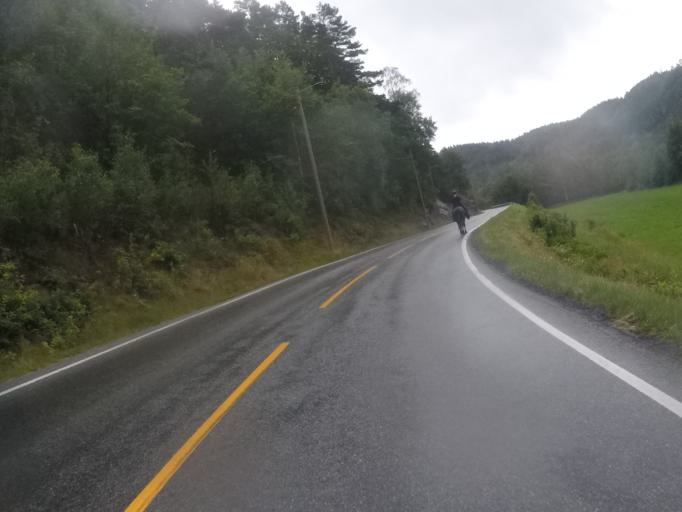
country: NO
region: Vest-Agder
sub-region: Songdalen
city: Nodeland
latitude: 58.1792
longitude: 7.8157
